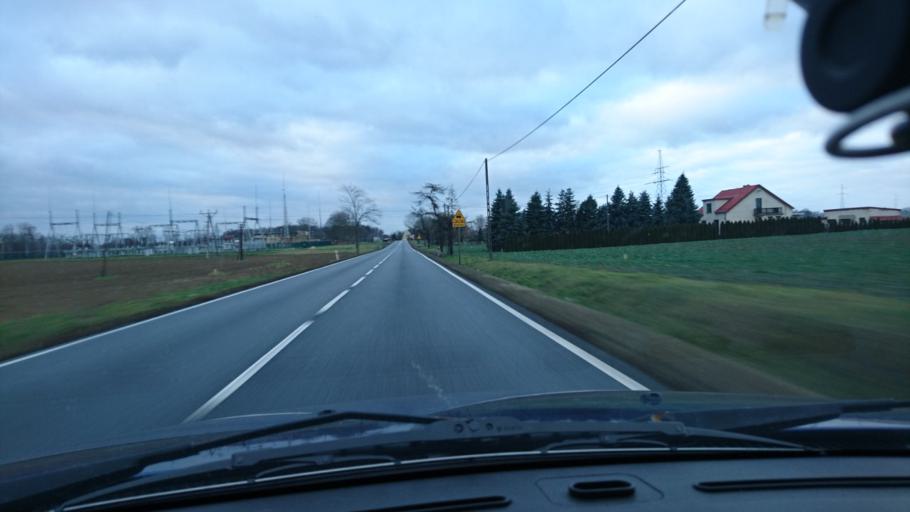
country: PL
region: Lodz Voivodeship
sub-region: Powiat wieruszowski
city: Boleslawiec
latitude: 51.1610
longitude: 18.1601
